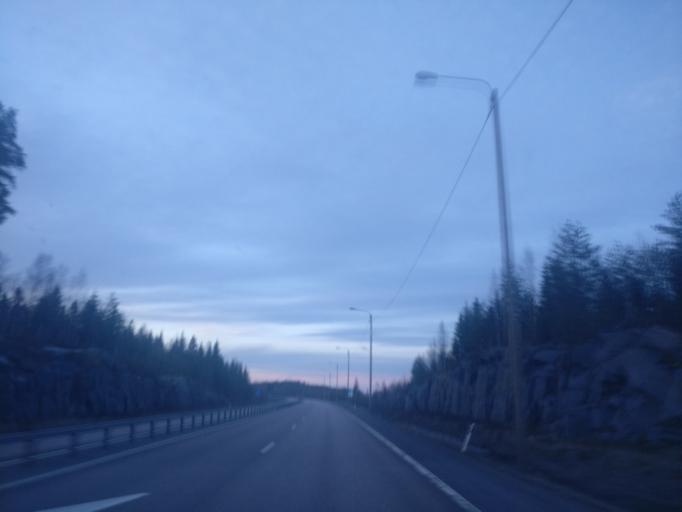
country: FI
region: Central Finland
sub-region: Jyvaeskylae
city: Saeynaetsalo
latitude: 62.1694
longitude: 25.9047
